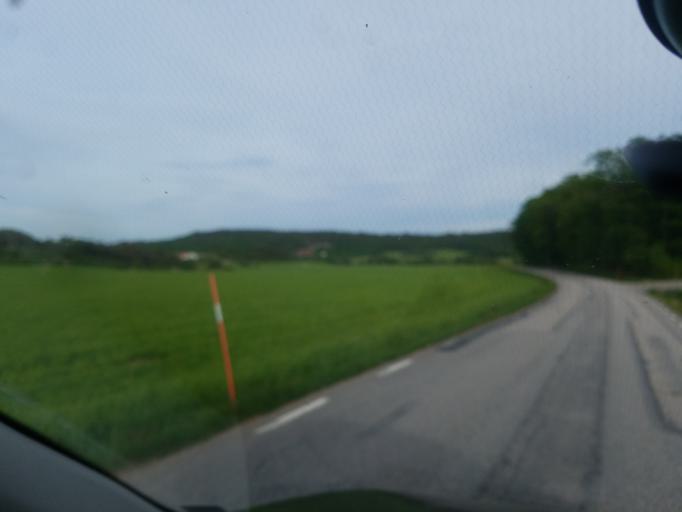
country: SE
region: Vaestra Goetaland
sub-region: Orust
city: Henan
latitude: 58.2804
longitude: 11.5882
